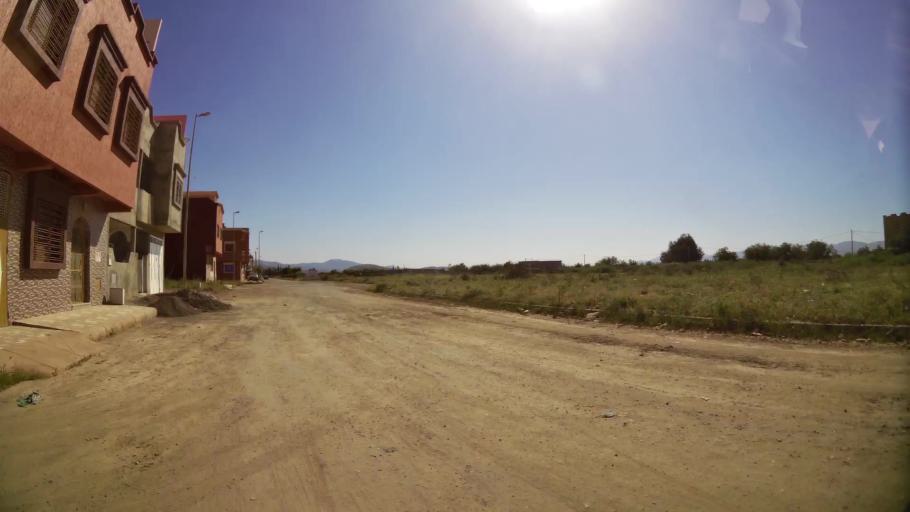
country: MA
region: Oriental
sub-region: Berkane-Taourirt
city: Berkane
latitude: 34.9435
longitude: -2.3402
